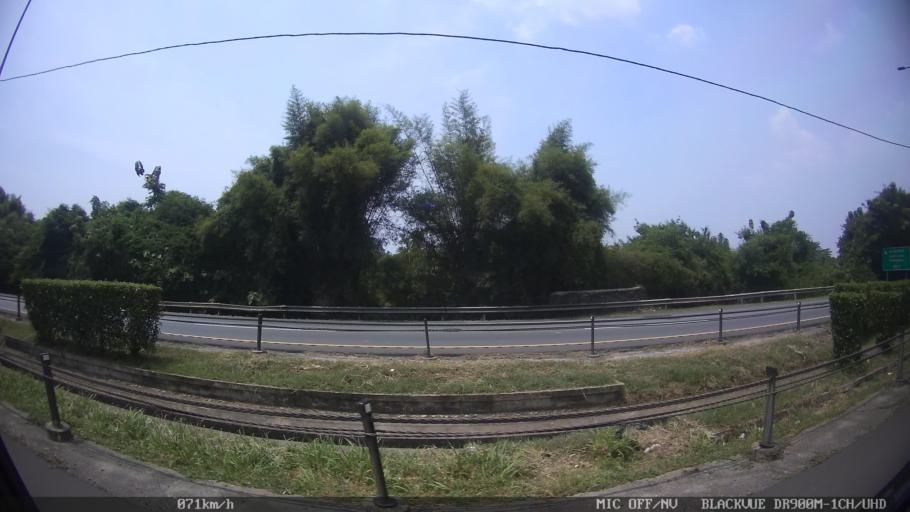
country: ID
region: Banten
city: Serang
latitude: -6.0858
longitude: 106.1380
